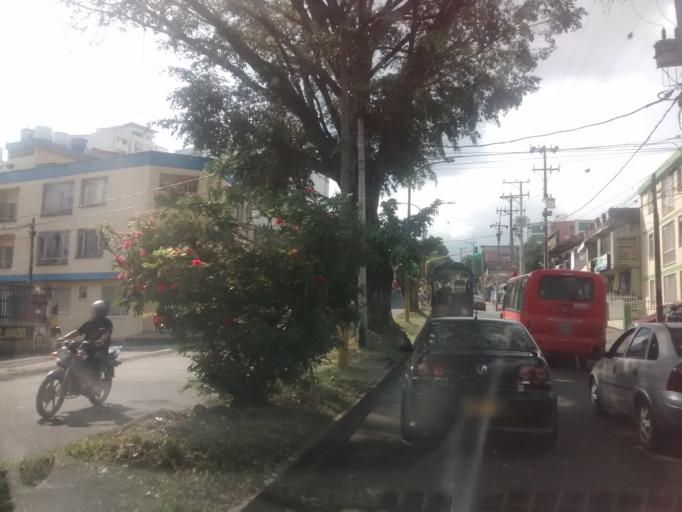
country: CO
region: Tolima
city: Ibague
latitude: 4.4462
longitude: -75.2351
